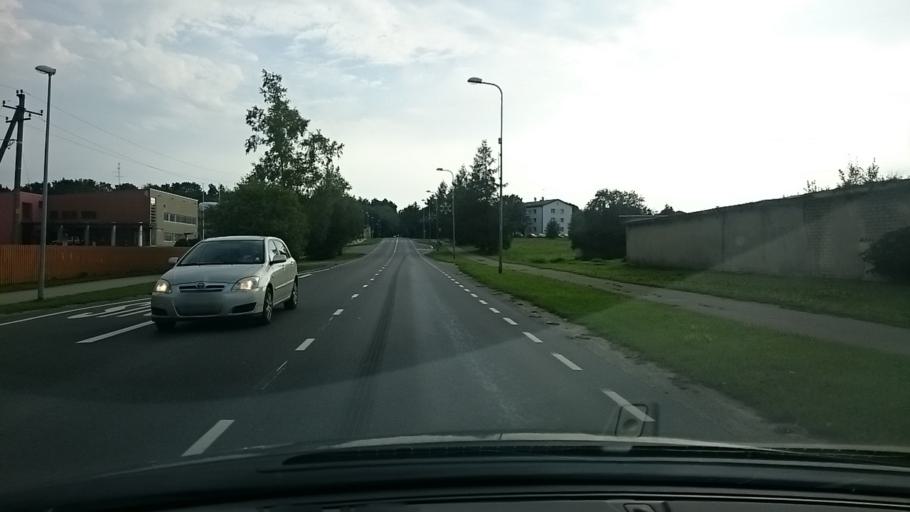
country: EE
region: Harju
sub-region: Saue vald
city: Laagri
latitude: 59.3896
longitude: 24.5799
